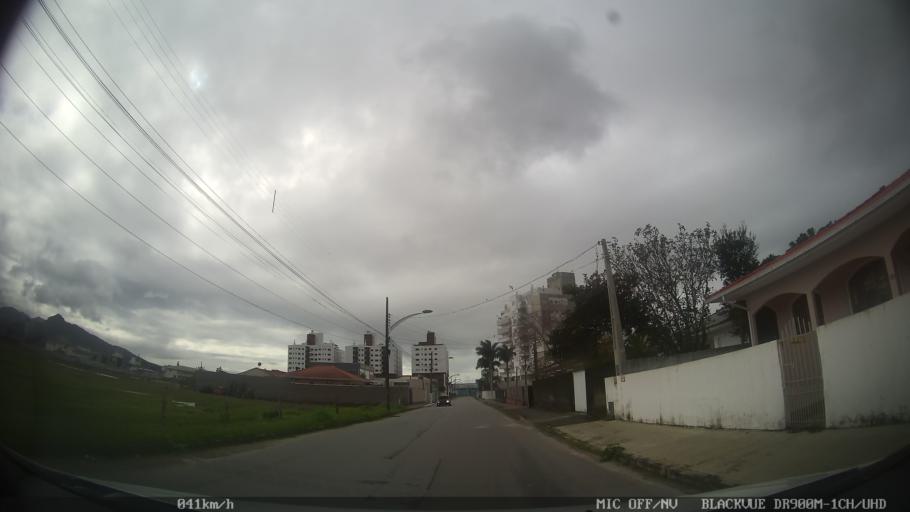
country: BR
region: Santa Catarina
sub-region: Biguacu
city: Biguacu
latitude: -27.5077
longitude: -48.6536
